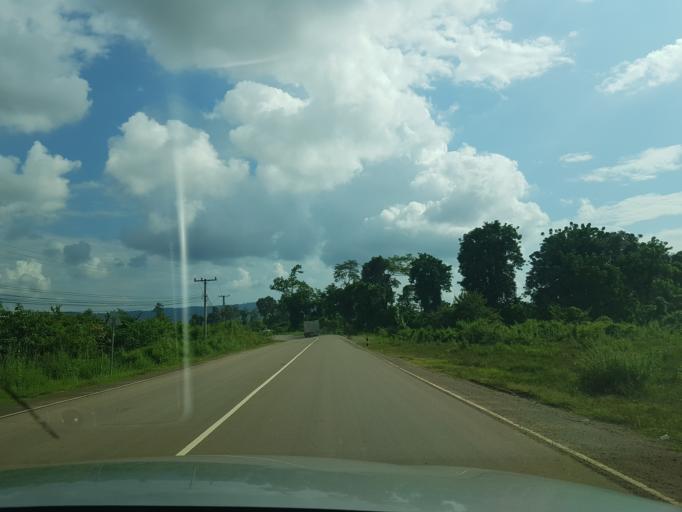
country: TH
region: Nong Khai
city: Sangkhom
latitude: 18.0888
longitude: 102.2907
